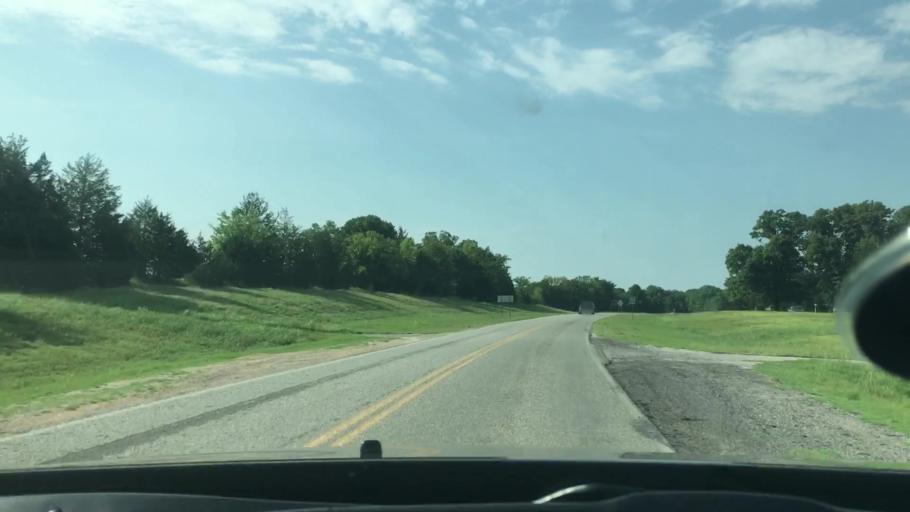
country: US
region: Oklahoma
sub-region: Johnston County
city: Tishomingo
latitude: 34.2296
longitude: -96.6348
